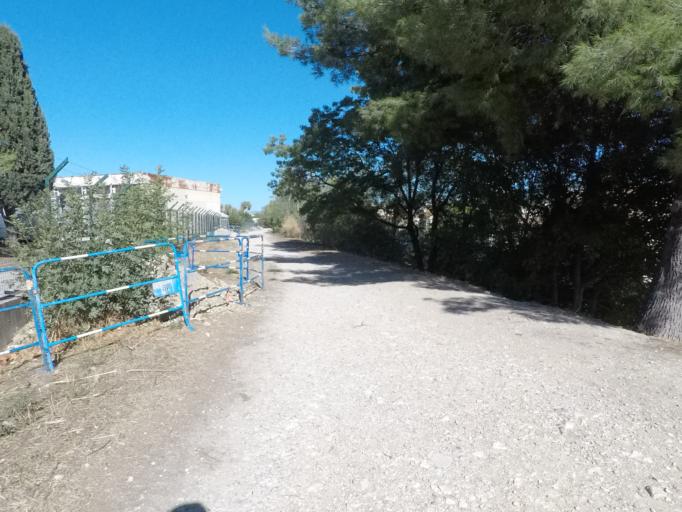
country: FR
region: Provence-Alpes-Cote d'Azur
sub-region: Departement des Bouches-du-Rhone
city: Marseille 10
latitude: 43.2724
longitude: 5.4053
